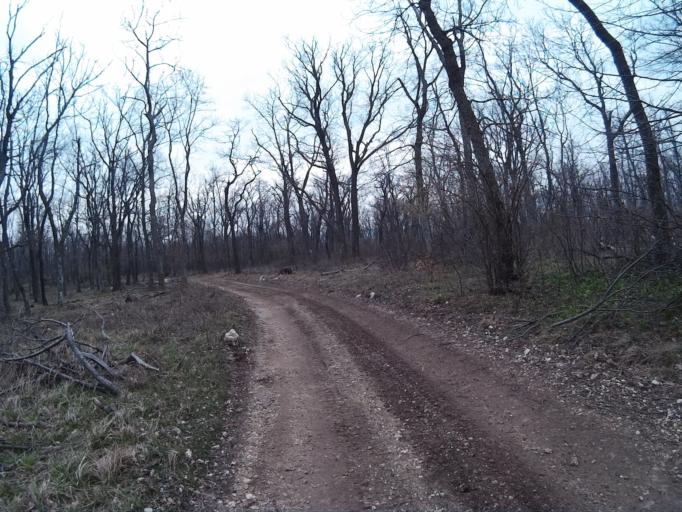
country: HU
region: Veszprem
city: Zirc
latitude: 47.1723
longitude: 17.8549
